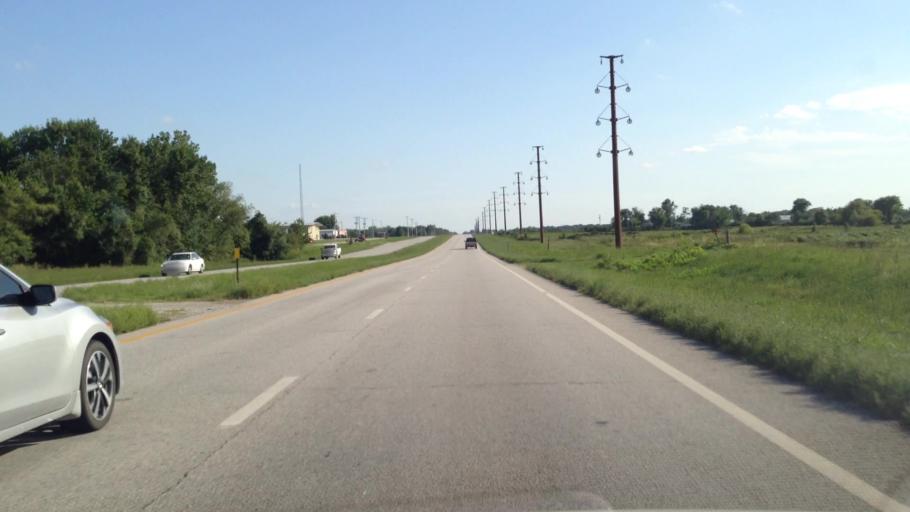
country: US
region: Kansas
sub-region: Crawford County
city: Frontenac
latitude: 37.4932
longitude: -94.7050
